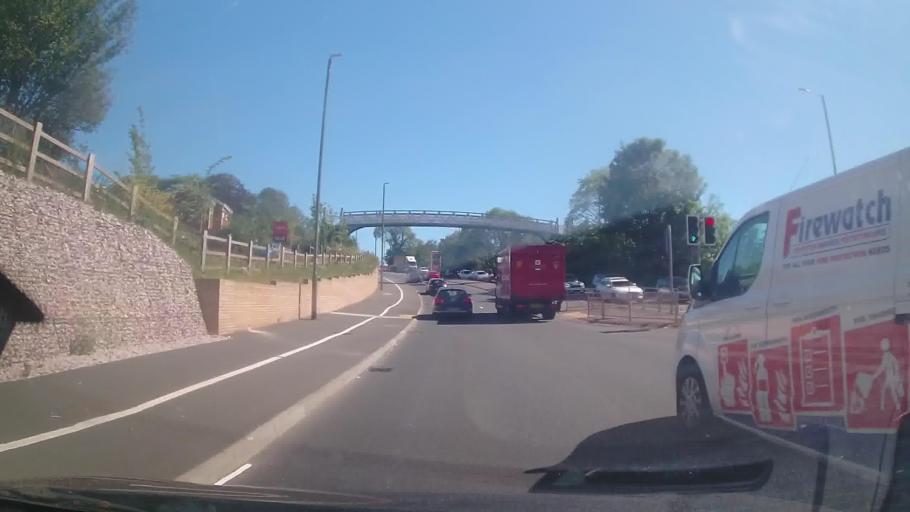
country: GB
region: England
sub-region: Borough of Torbay
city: Paignton
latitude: 50.4222
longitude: -3.5872
